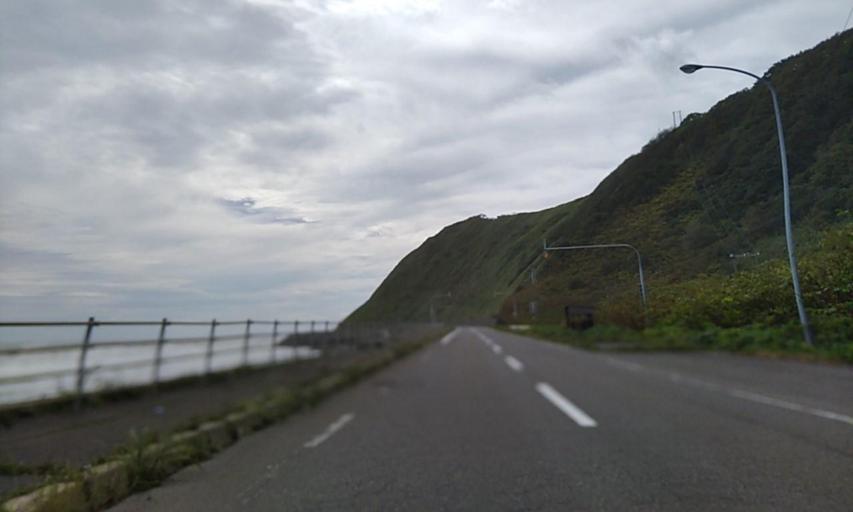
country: JP
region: Hokkaido
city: Kushiro
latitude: 42.7952
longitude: 143.8055
